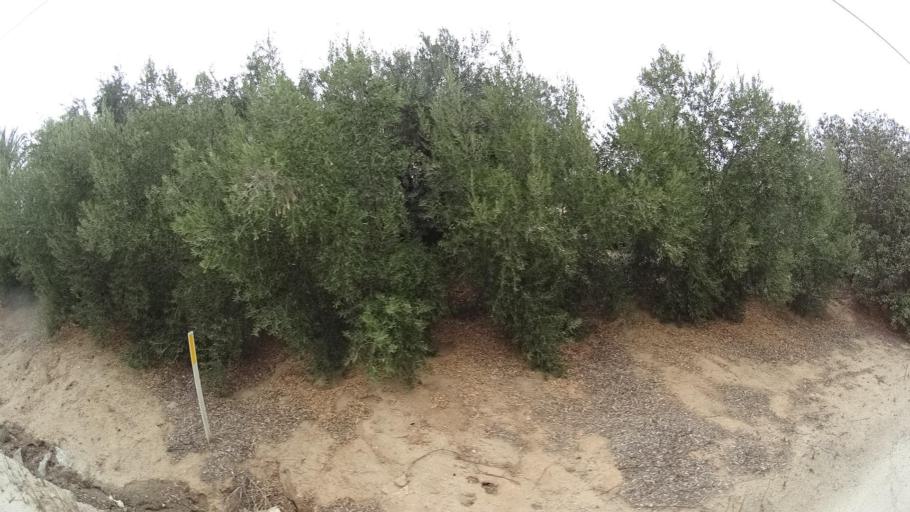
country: US
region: California
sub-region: San Diego County
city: Ramona
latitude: 33.0549
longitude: -116.8620
